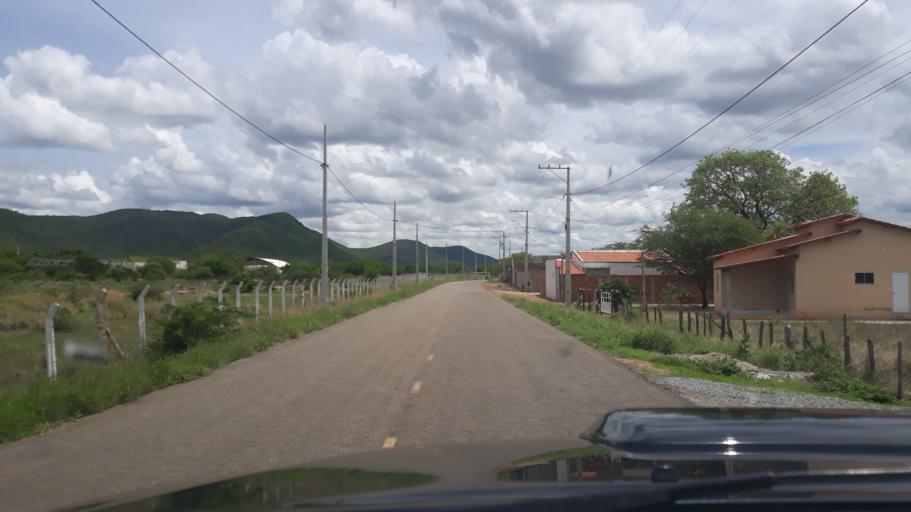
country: BR
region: Bahia
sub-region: Guanambi
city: Guanambi
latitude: -14.2989
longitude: -42.6959
